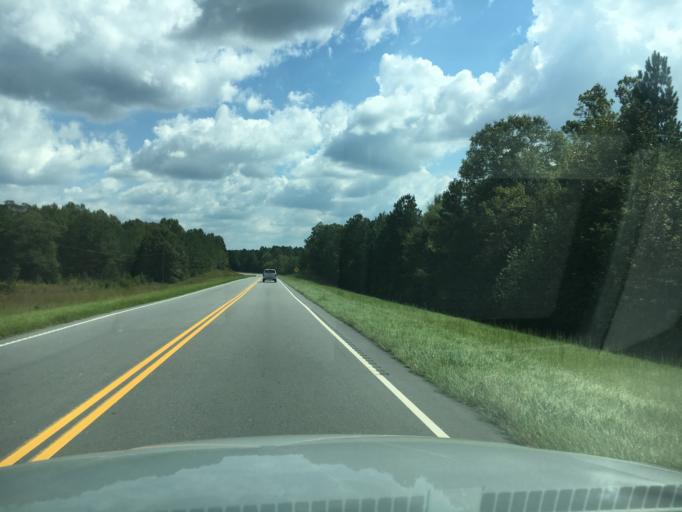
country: US
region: South Carolina
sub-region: Greenwood County
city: Greenwood
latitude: 34.1399
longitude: -82.1448
